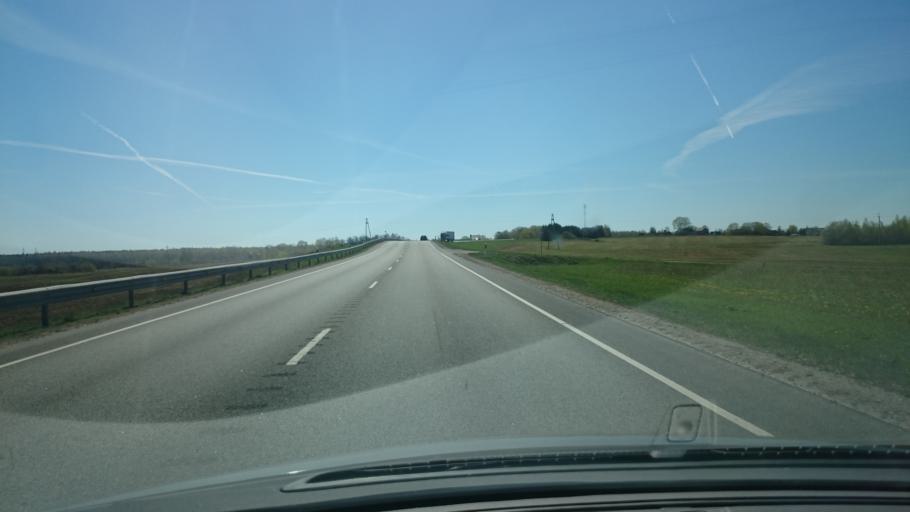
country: EE
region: Ida-Virumaa
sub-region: Narva-Joesuu linn
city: Narva-Joesuu
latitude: 59.3932
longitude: 27.9930
